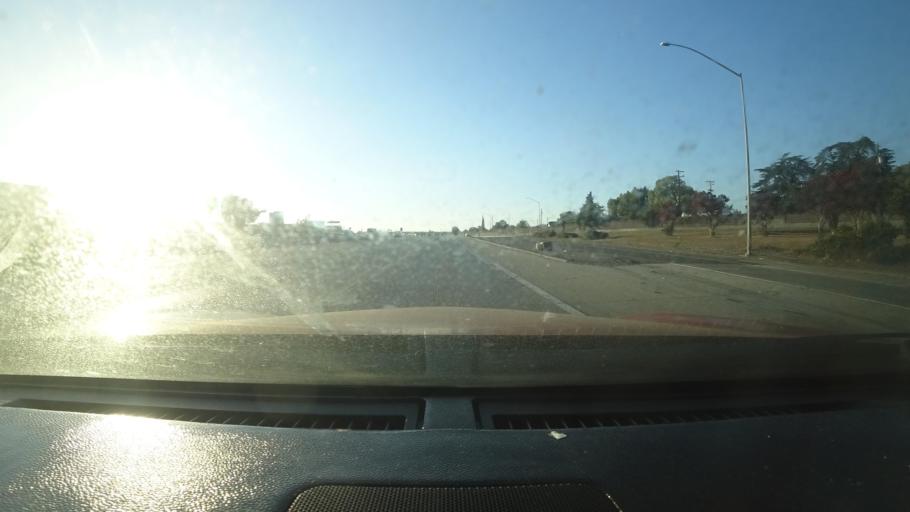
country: US
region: California
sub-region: Santa Clara County
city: San Jose
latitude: 37.3500
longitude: -121.8615
